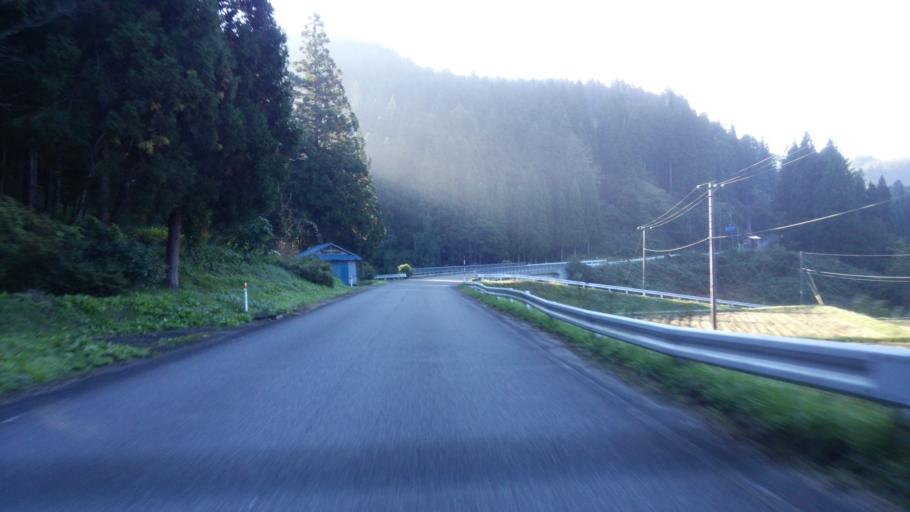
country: JP
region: Fukushima
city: Kitakata
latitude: 37.4295
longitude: 139.7258
